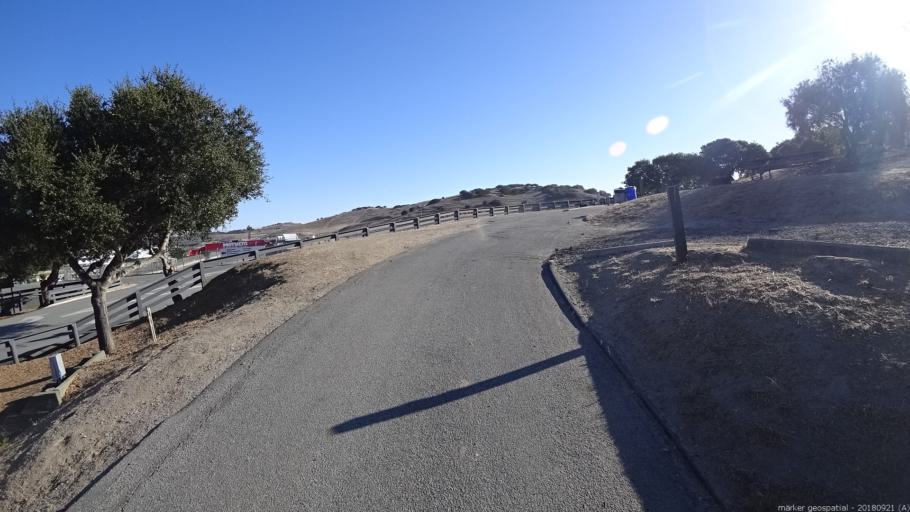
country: US
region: California
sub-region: Monterey County
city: Carmel Valley Village
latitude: 36.5794
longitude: -121.7546
